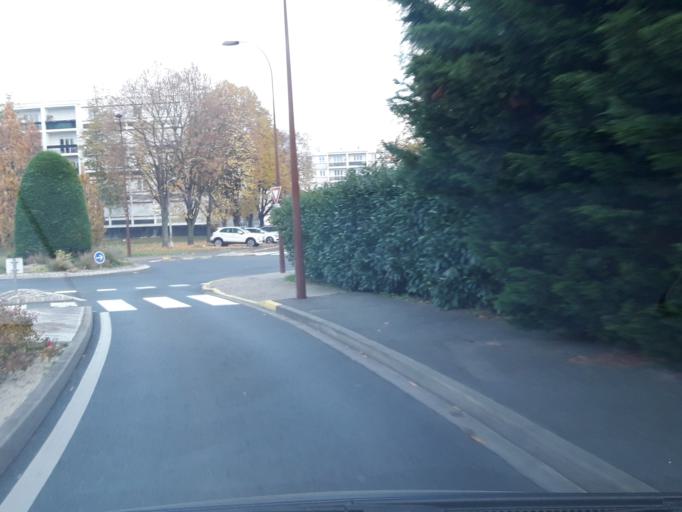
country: FR
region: Ile-de-France
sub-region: Departement de l'Essonne
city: Fleury-Merogis
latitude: 48.6418
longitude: 2.3498
